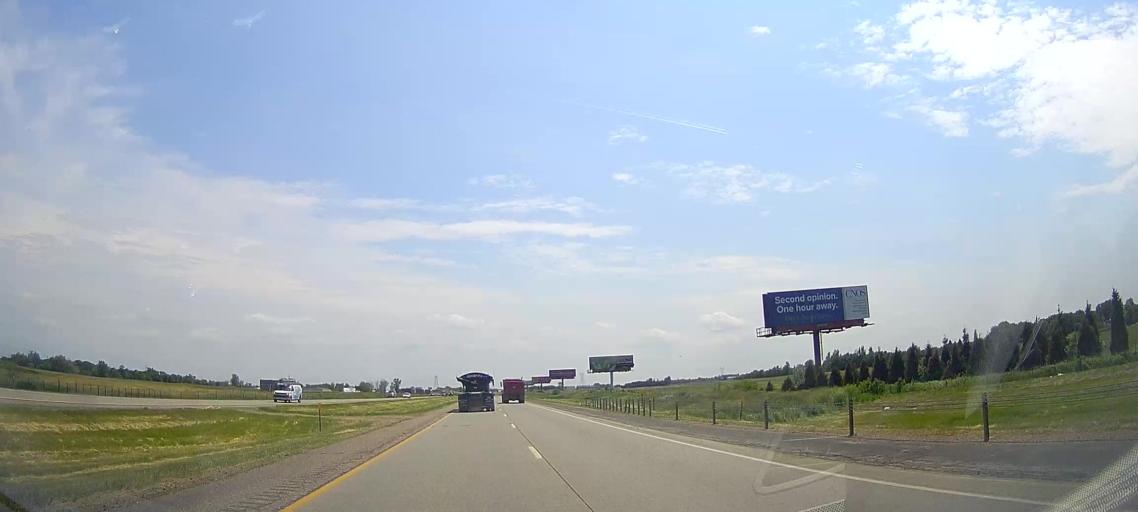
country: US
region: South Dakota
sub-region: Lincoln County
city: Tea
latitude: 43.4452
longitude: -96.7976
